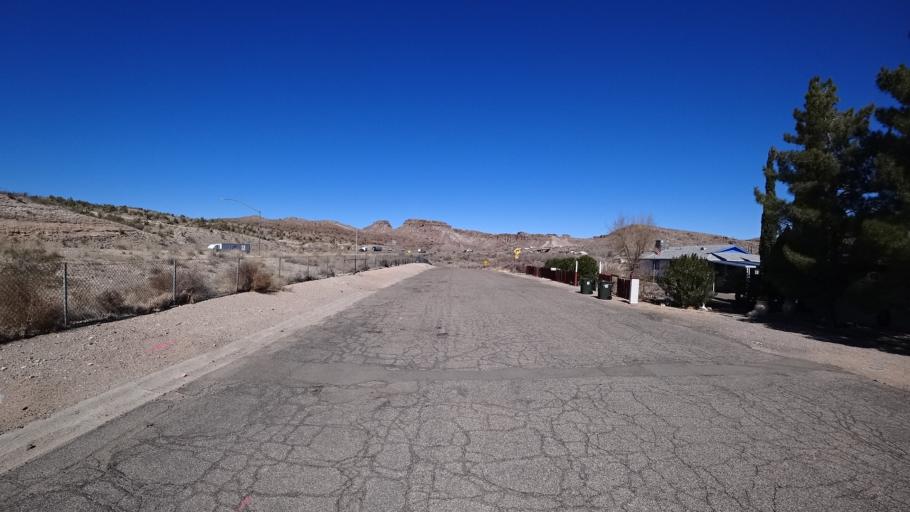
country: US
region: Arizona
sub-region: Mohave County
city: Kingman
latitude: 35.1955
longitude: -114.0664
